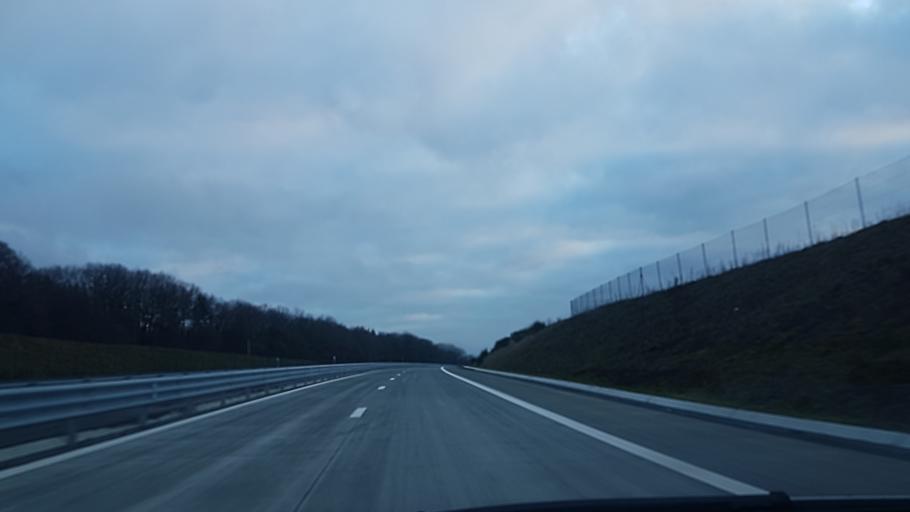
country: FR
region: Champagne-Ardenne
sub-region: Departement des Ardennes
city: Rocroi
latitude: 49.9958
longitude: 4.5429
